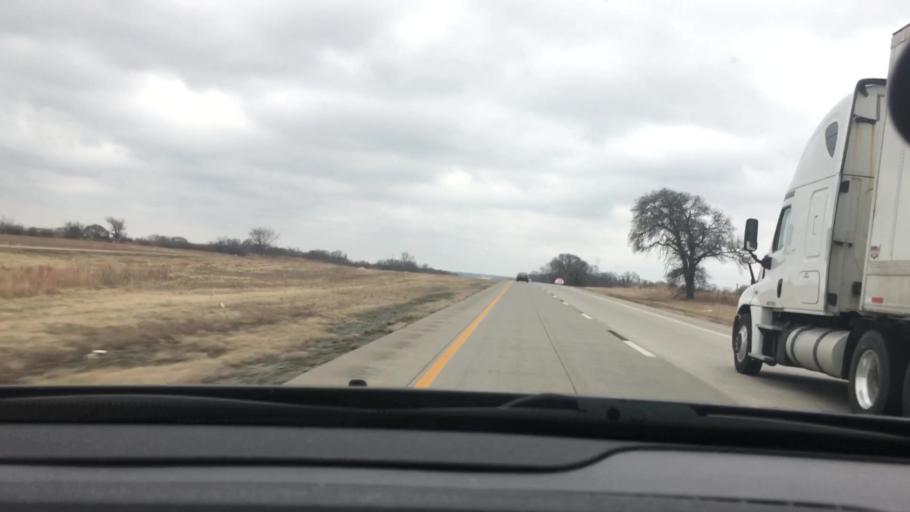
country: US
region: Oklahoma
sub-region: Atoka County
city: Atoka
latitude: 34.2218
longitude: -96.2276
